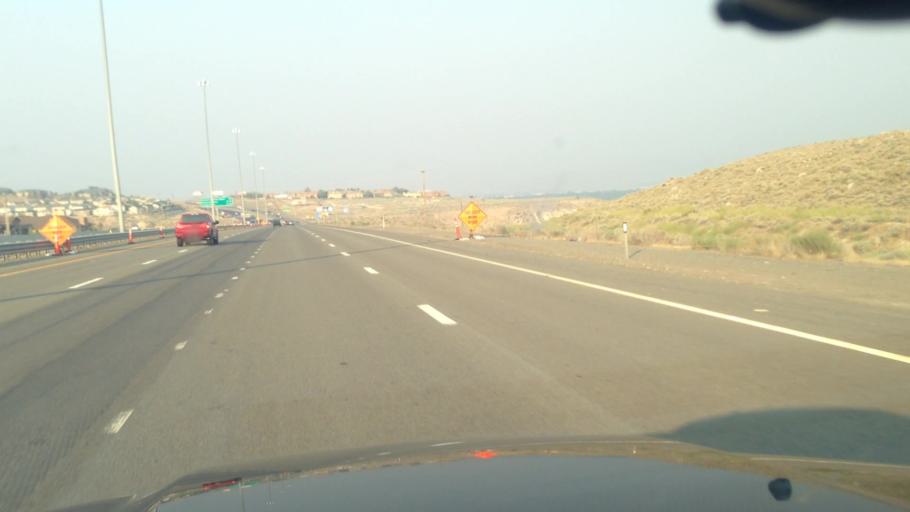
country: US
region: Nevada
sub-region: Washoe County
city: Mogul
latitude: 39.5161
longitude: -119.8852
